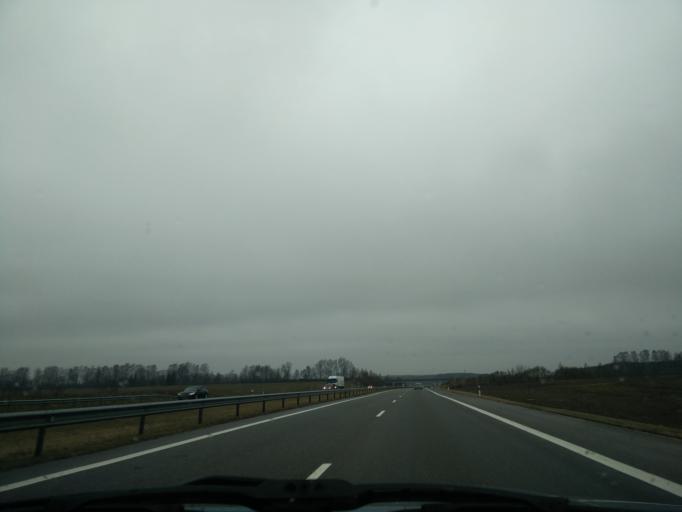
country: LT
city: Skaudvile
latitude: 55.4047
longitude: 22.8457
